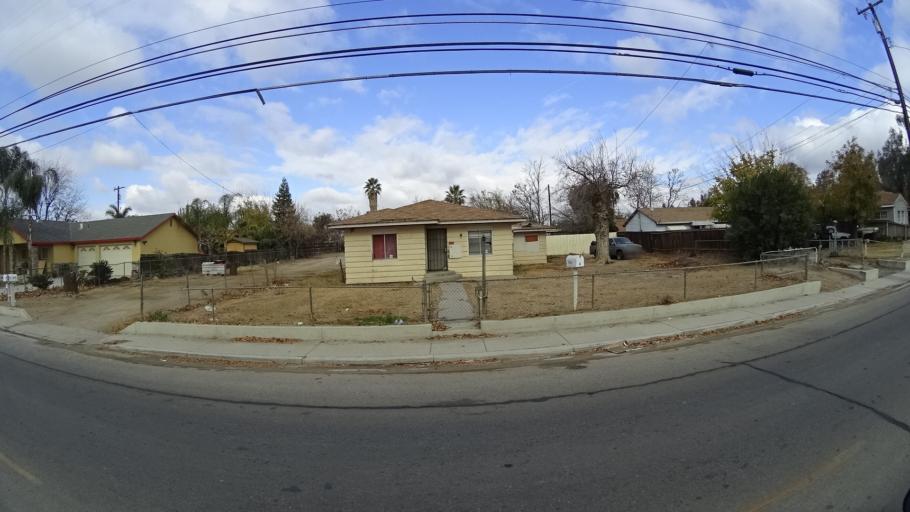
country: US
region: California
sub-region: Kern County
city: Bakersfield
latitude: 35.3395
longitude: -118.9980
